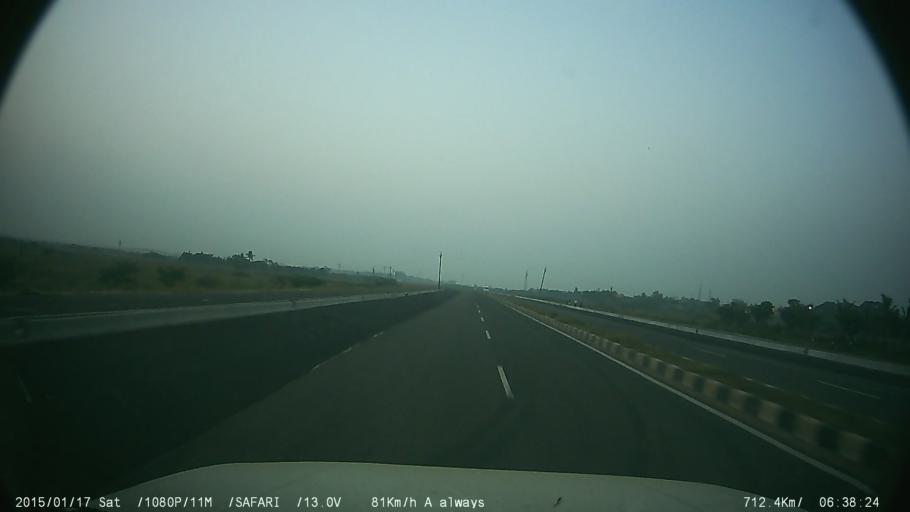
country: IN
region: Tamil Nadu
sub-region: Kancheepuram
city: Sriperumbudur
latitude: 12.9360
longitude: 79.9354
